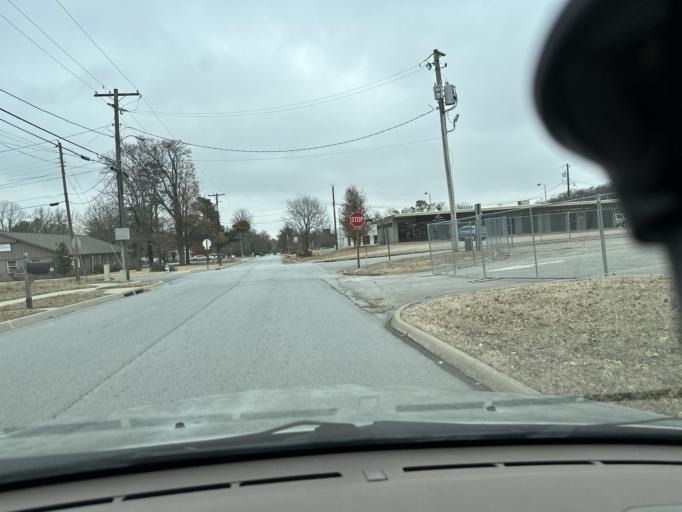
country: US
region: Arkansas
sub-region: Washington County
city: Fayetteville
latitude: 36.0883
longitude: -94.1555
